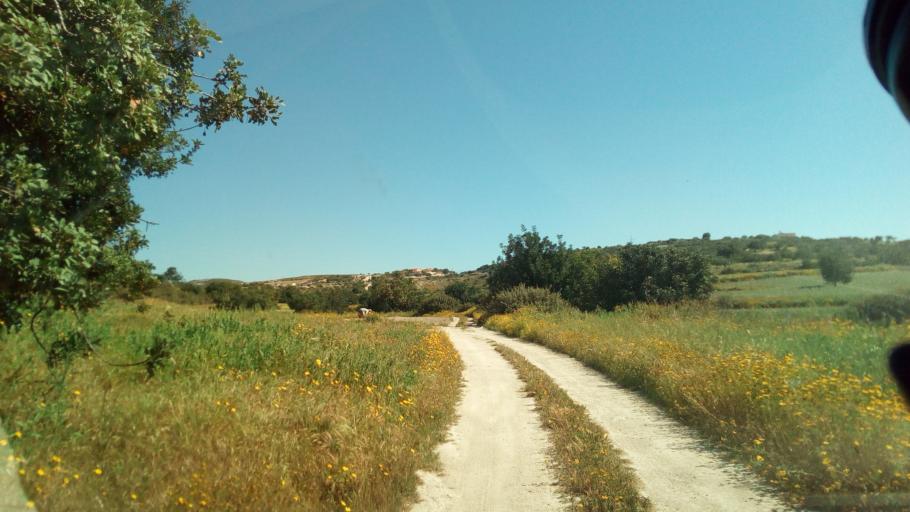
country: CY
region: Limassol
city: Pissouri
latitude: 34.6746
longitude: 32.6879
